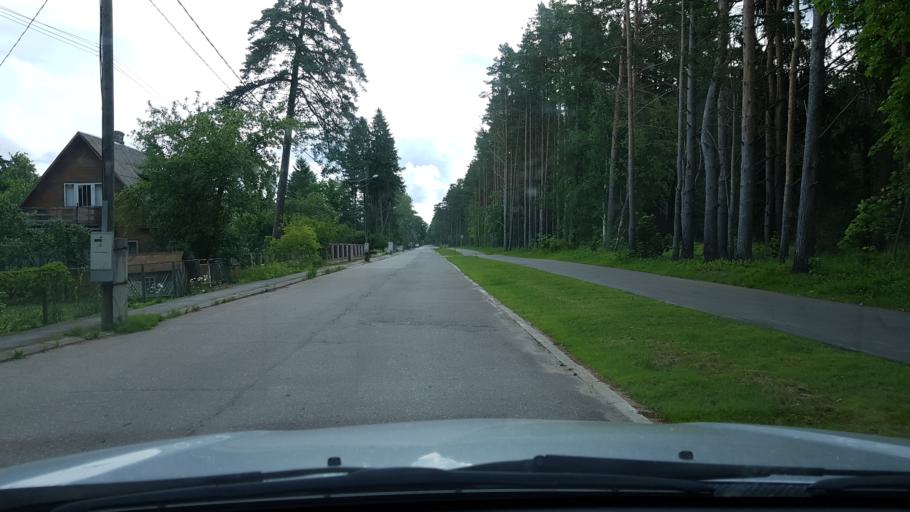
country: EE
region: Ida-Virumaa
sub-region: Narva-Joesuu linn
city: Narva-Joesuu
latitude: 59.4492
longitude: 28.0293
